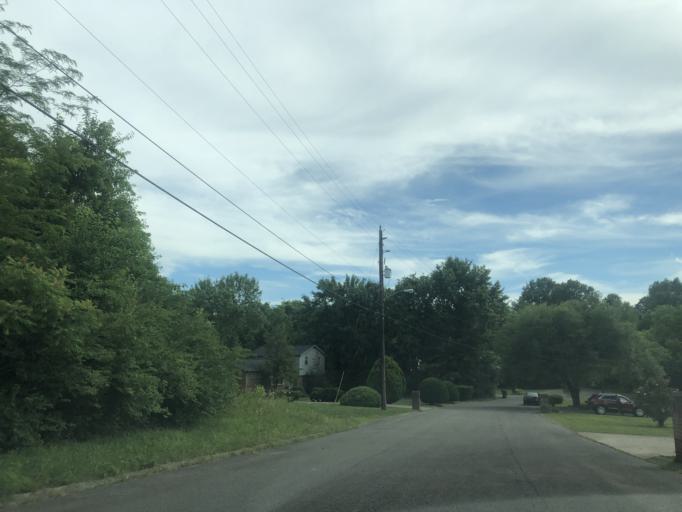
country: US
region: Tennessee
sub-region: Davidson County
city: Nashville
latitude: 36.2169
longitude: -86.8072
